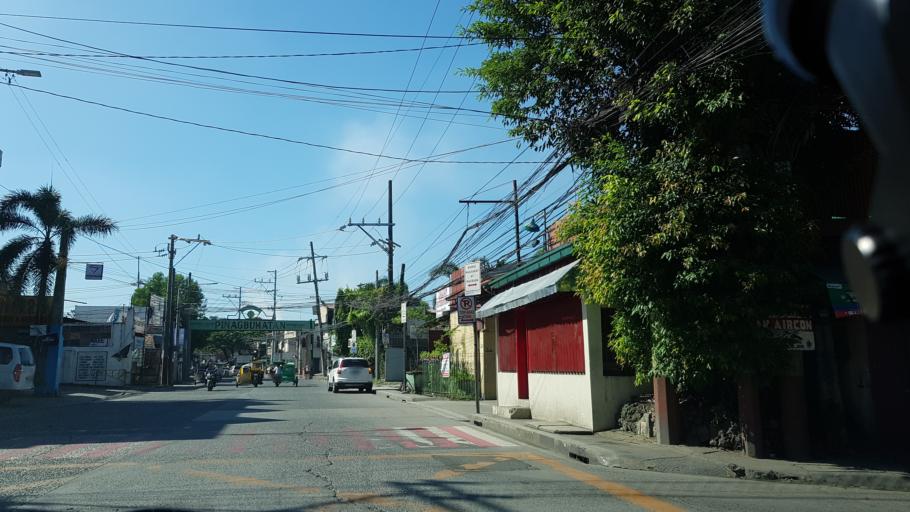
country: PH
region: Calabarzon
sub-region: Province of Rizal
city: Pateros
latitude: 14.5623
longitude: 121.0940
